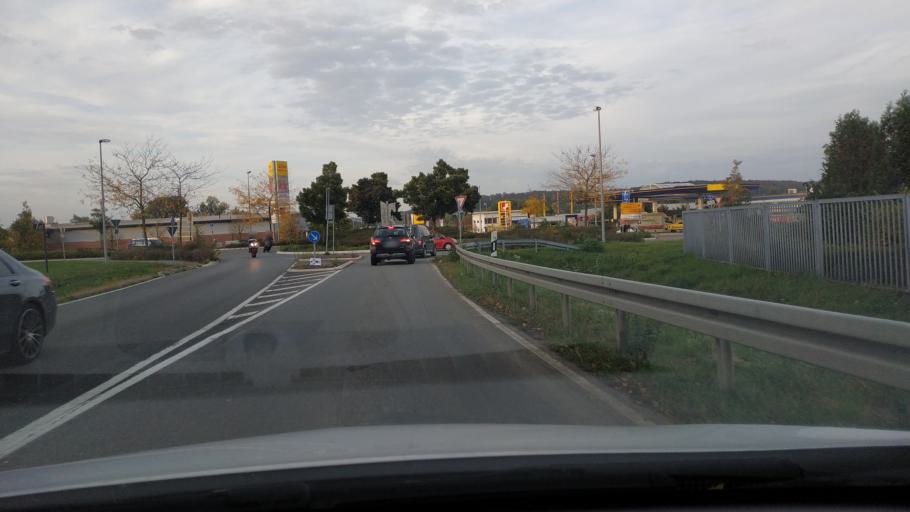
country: DE
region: Lower Saxony
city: Bissendorf
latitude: 52.2367
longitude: 8.1625
